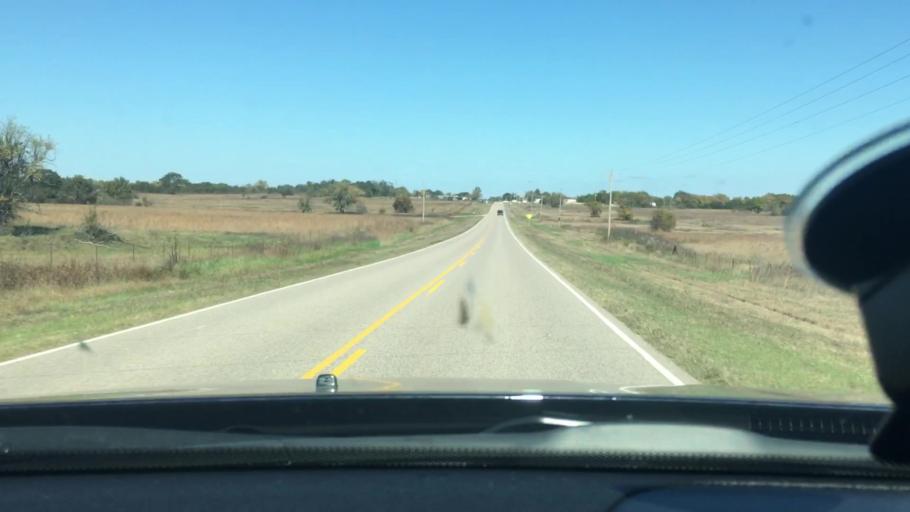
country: US
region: Oklahoma
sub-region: Johnston County
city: Tishomingo
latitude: 34.4345
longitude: -96.6360
